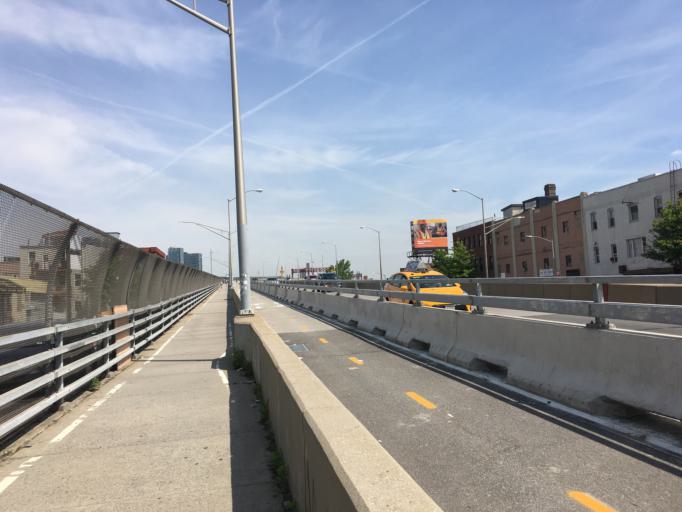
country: US
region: New York
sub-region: Queens County
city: Long Island City
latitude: 40.7359
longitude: -73.9528
